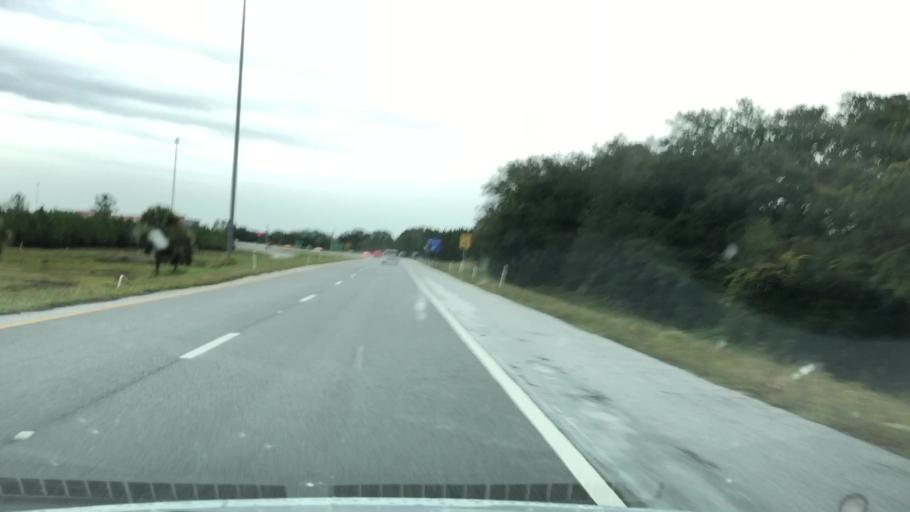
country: US
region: Florida
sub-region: Seminole County
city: Heathrow
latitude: 28.7527
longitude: -81.3624
